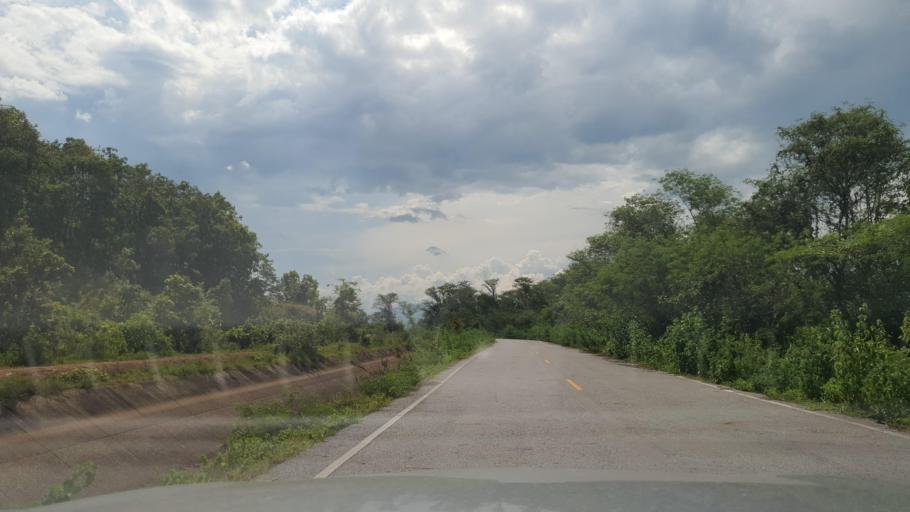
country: TH
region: Chiang Mai
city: San Kamphaeng
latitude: 18.7735
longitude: 99.1776
